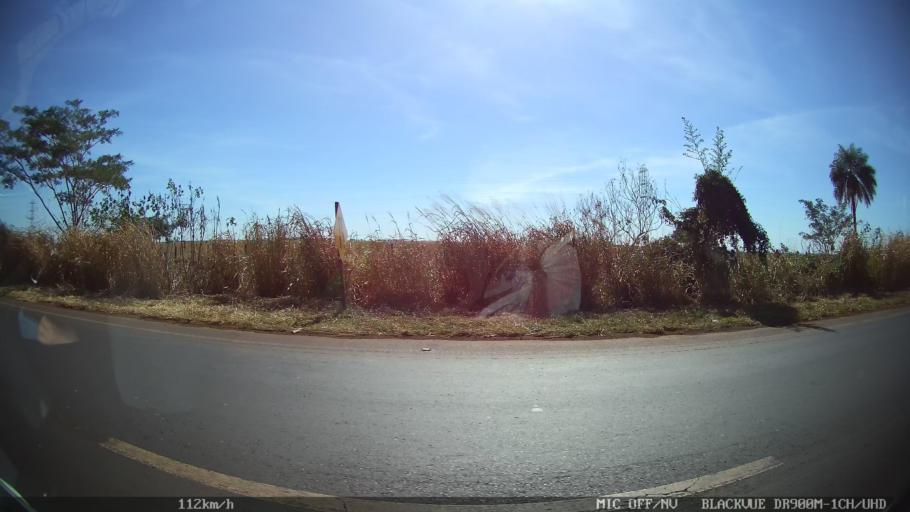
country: BR
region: Sao Paulo
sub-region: Barretos
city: Barretos
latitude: -20.4936
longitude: -48.5278
